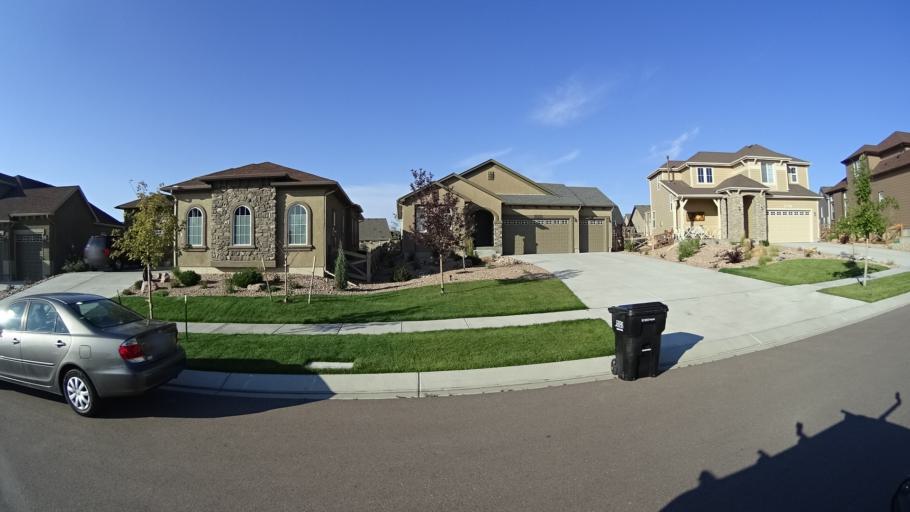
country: US
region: Colorado
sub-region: El Paso County
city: Cimarron Hills
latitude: 38.9360
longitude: -104.6594
